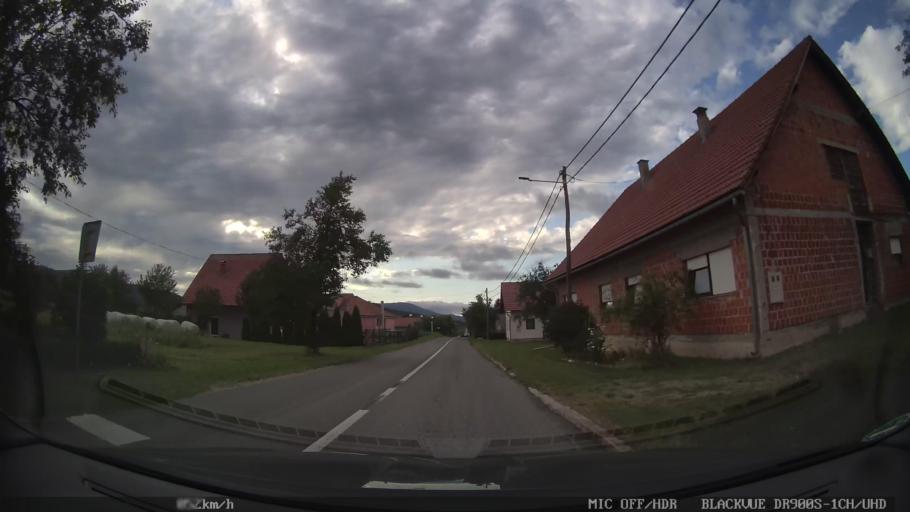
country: HR
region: Karlovacka
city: Plaski
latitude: 44.9830
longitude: 15.4800
